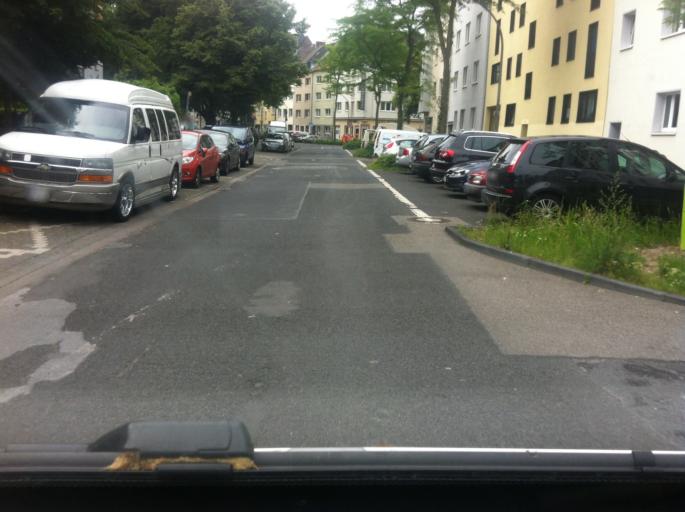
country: DE
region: North Rhine-Westphalia
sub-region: Regierungsbezirk Koln
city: Neuehrenfeld
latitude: 50.9438
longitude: 6.9236
